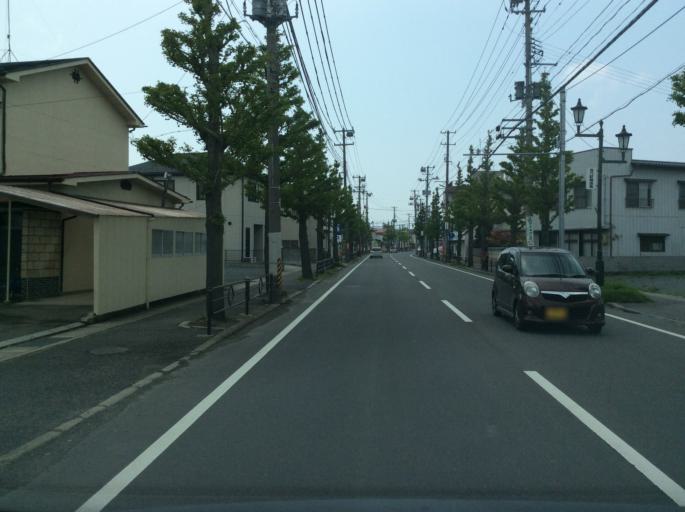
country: JP
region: Fukushima
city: Koriyama
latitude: 37.3884
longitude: 140.3980
